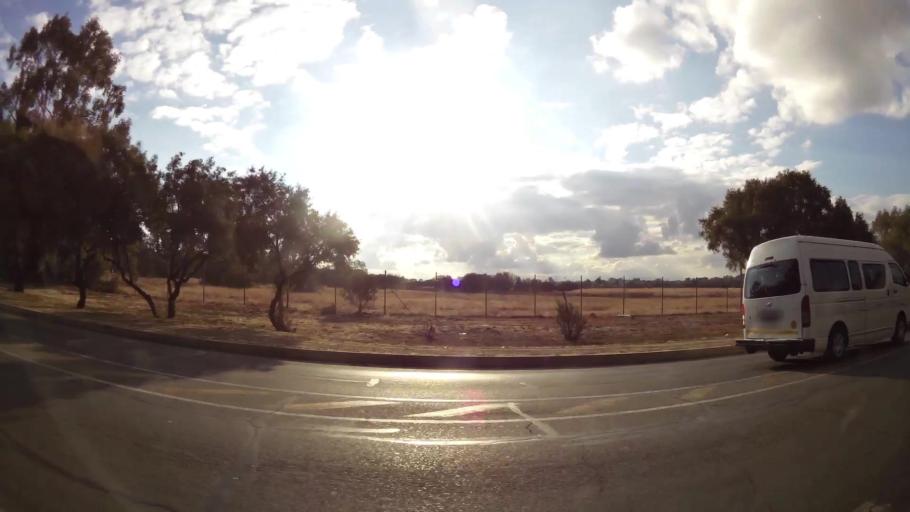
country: ZA
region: Orange Free State
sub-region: Mangaung Metropolitan Municipality
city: Bloemfontein
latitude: -29.1013
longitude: 26.1860
